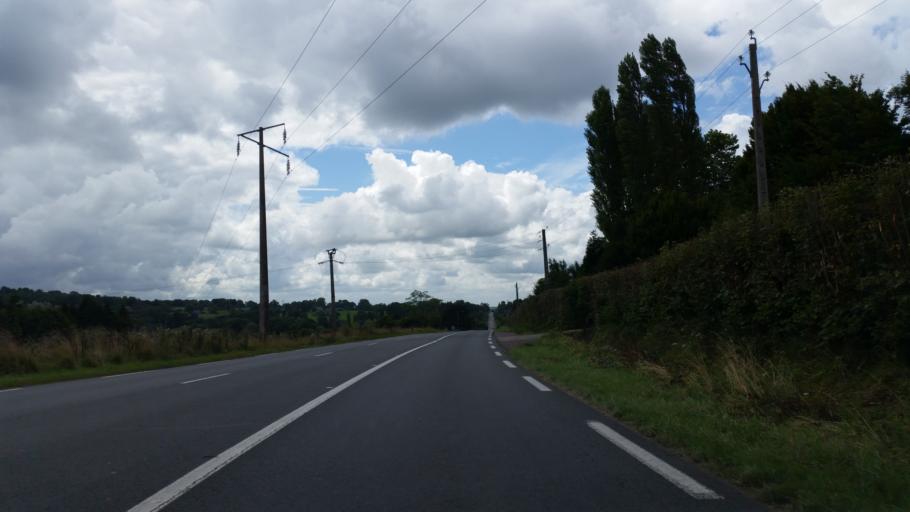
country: FR
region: Lower Normandy
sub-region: Departement du Calvados
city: Saint-Gatien-des-Bois
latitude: 49.3254
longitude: 0.2001
